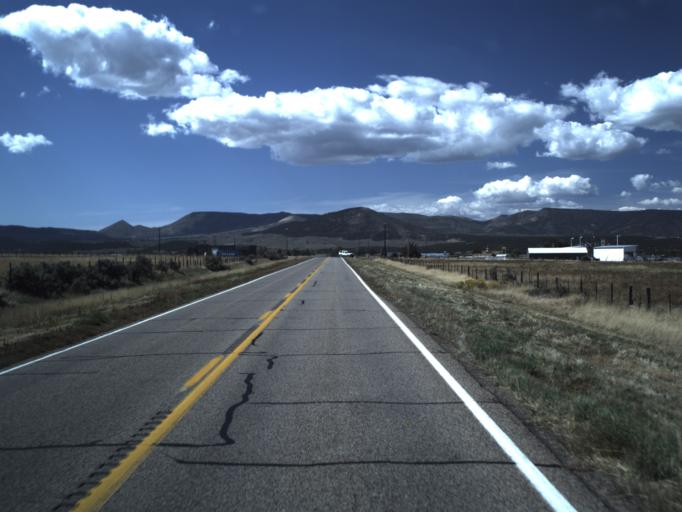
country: US
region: Utah
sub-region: Washington County
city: Enterprise
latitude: 37.5773
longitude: -113.6957
